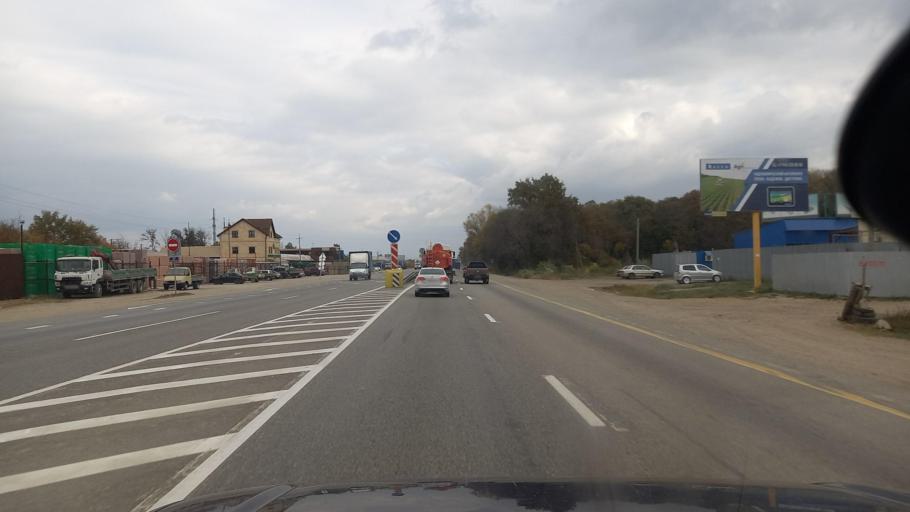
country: RU
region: Krasnodarskiy
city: Afipskiy
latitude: 44.9041
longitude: 38.8748
